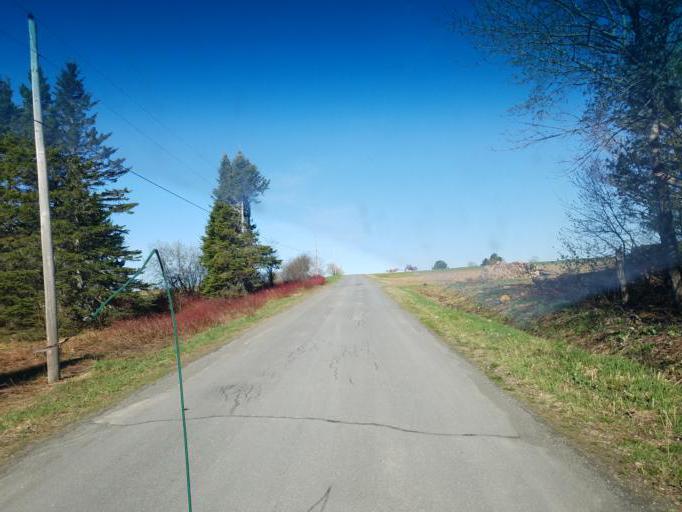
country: US
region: Maine
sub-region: Aroostook County
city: Caribou
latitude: 46.8672
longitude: -68.2033
